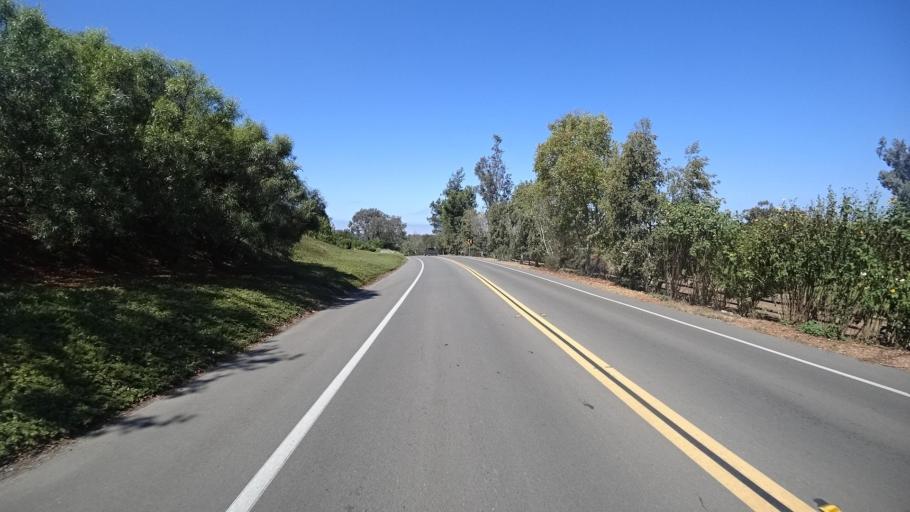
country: US
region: California
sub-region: San Diego County
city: Rancho Santa Fe
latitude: 33.0236
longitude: -117.2165
